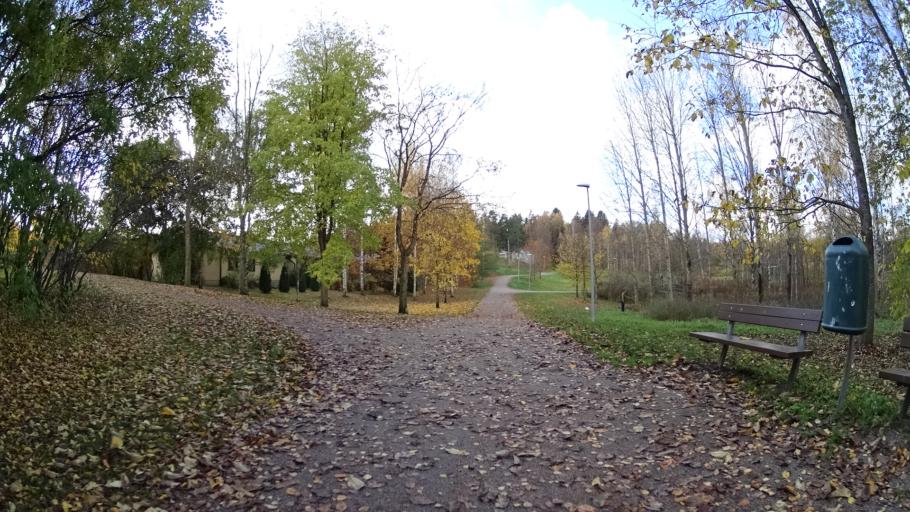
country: FI
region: Uusimaa
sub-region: Helsinki
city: Kilo
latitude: 60.2661
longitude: 24.7956
